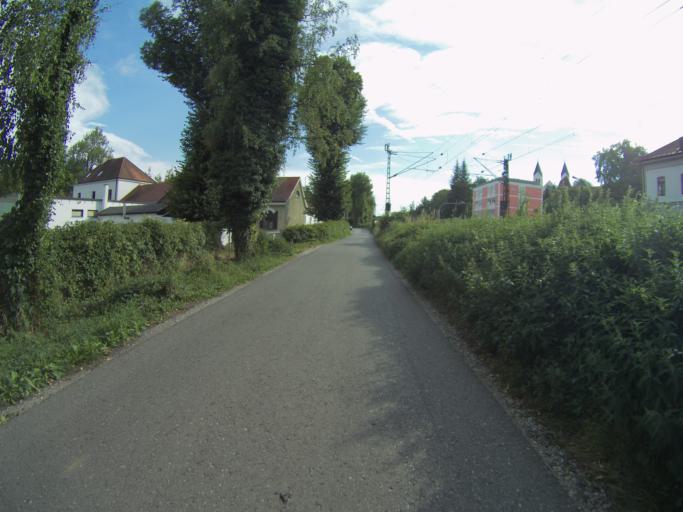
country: DE
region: Bavaria
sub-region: Upper Bavaria
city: Freising
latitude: 48.4009
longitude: 11.7519
